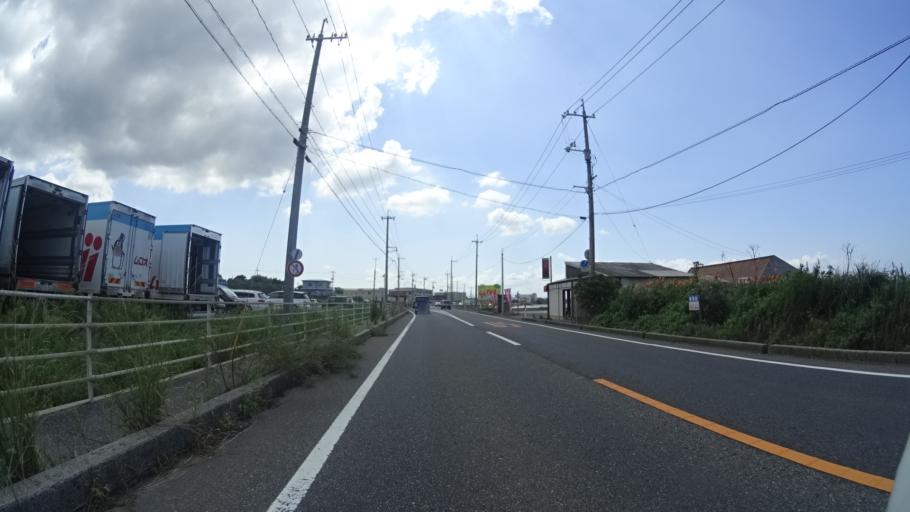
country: JP
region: Yamaguchi
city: Shimonoseki
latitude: 34.0483
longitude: 130.9147
